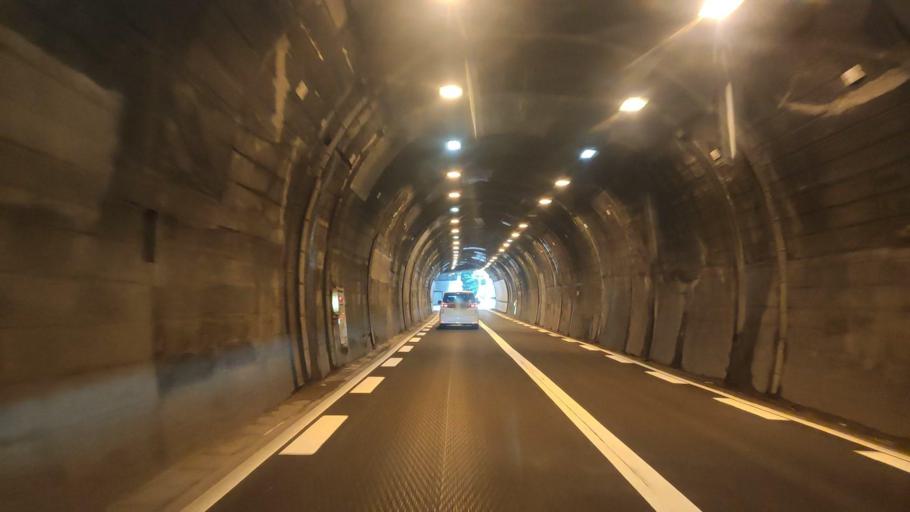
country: JP
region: Fukui
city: Takefu
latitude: 35.7849
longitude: 136.1007
